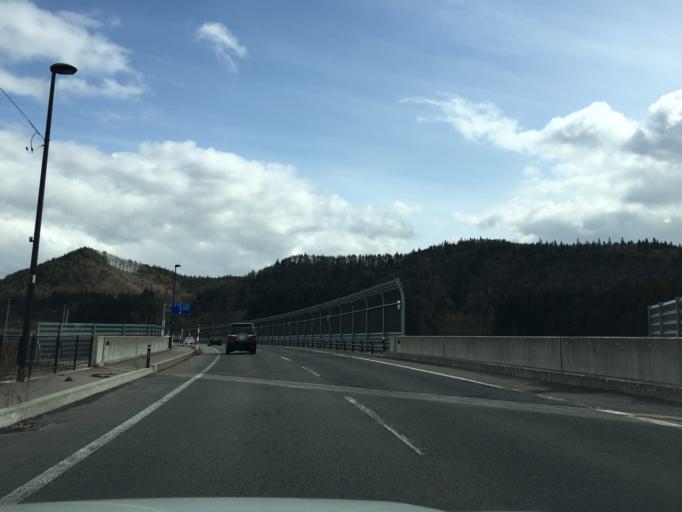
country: JP
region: Akita
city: Hanawa
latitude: 40.2242
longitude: 140.7170
